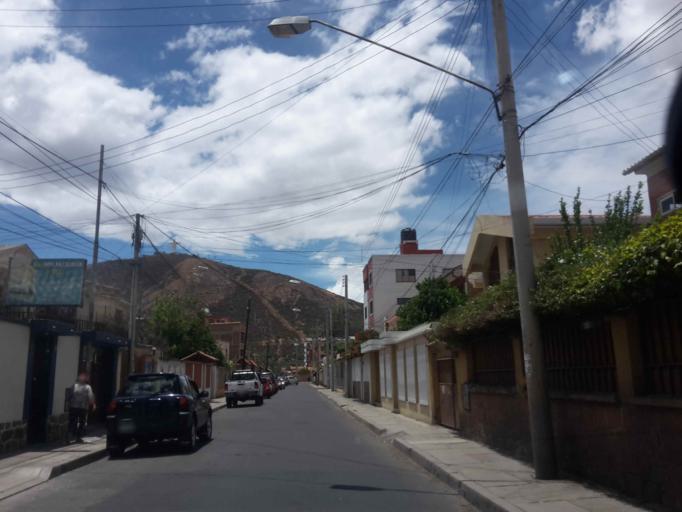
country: BO
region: Cochabamba
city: Cochabamba
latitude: -17.3892
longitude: -66.1473
